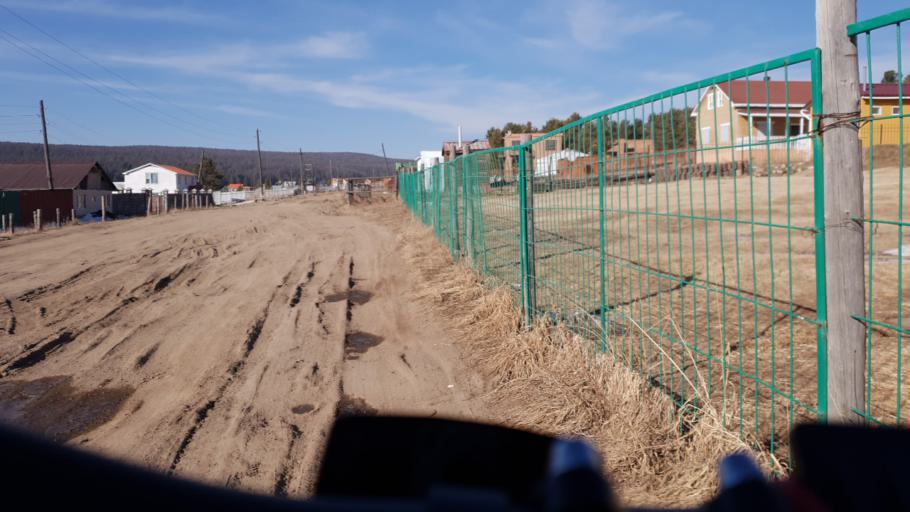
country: MN
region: Ulaanbaatar
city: Ulaanbaatar
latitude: 48.1522
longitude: 106.8841
